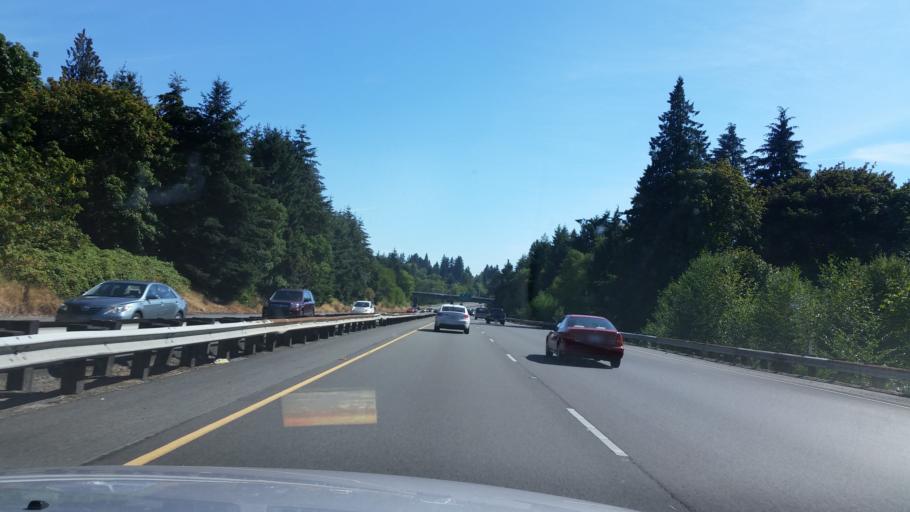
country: US
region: Washington
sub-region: King County
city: Boulevard Park
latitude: 47.4848
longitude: -122.3274
